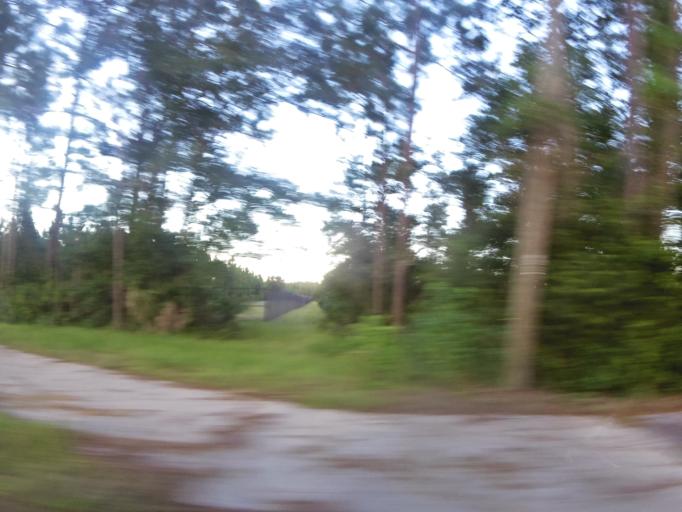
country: US
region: Georgia
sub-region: Camden County
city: St Marys
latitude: 30.7687
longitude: -81.5764
